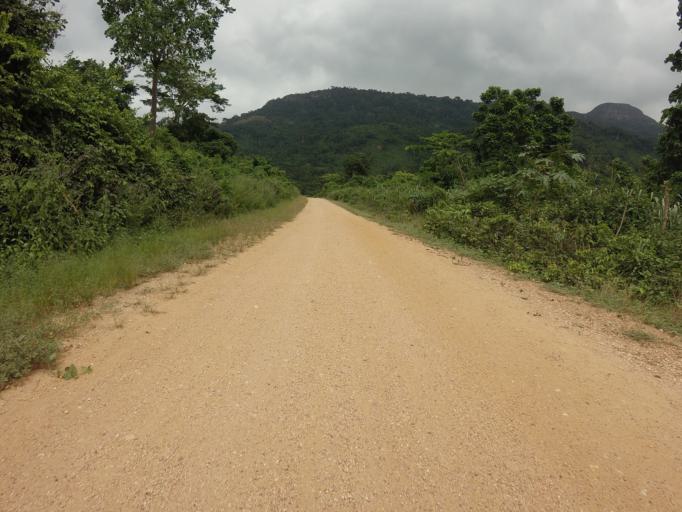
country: GH
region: Volta
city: Kpandu
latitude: 6.8726
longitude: 0.4242
